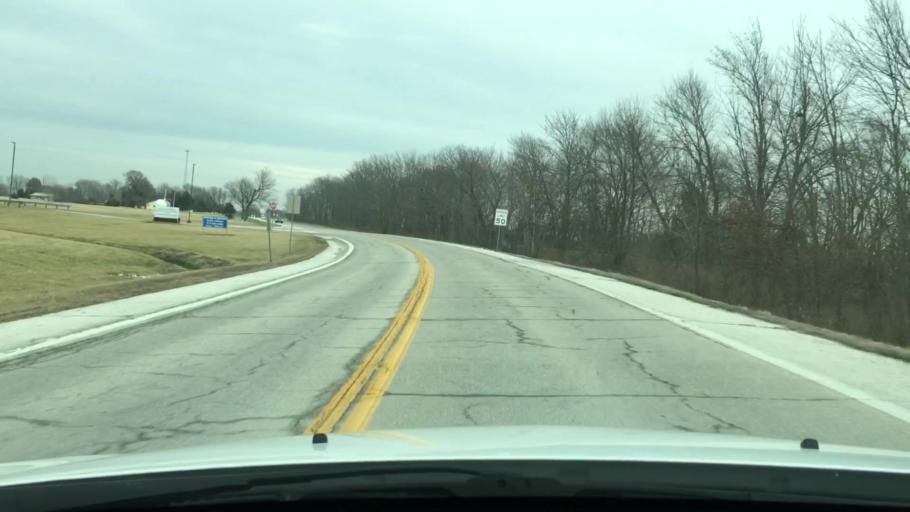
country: US
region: Missouri
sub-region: Audrain County
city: Vandalia
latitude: 39.3141
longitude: -91.4774
